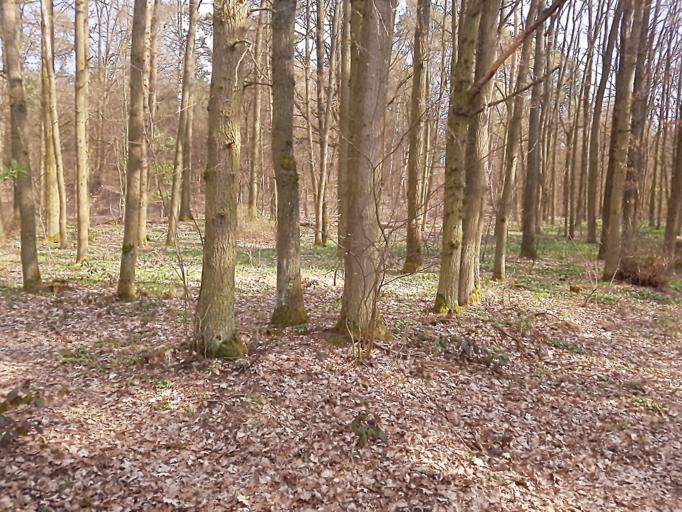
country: DE
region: Bavaria
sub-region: Upper Franconia
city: Breitengussbach
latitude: 49.9629
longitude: 10.8935
